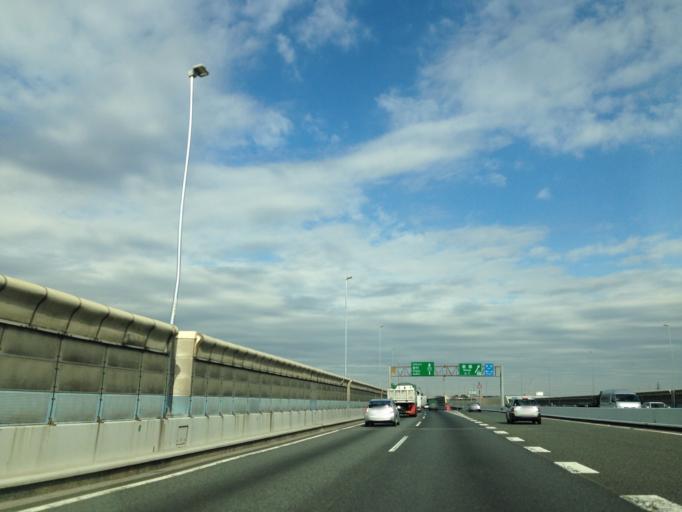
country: JP
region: Saitama
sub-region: Kawaguchi-shi
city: Hatogaya-honcho
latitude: 35.8156
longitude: 139.7596
